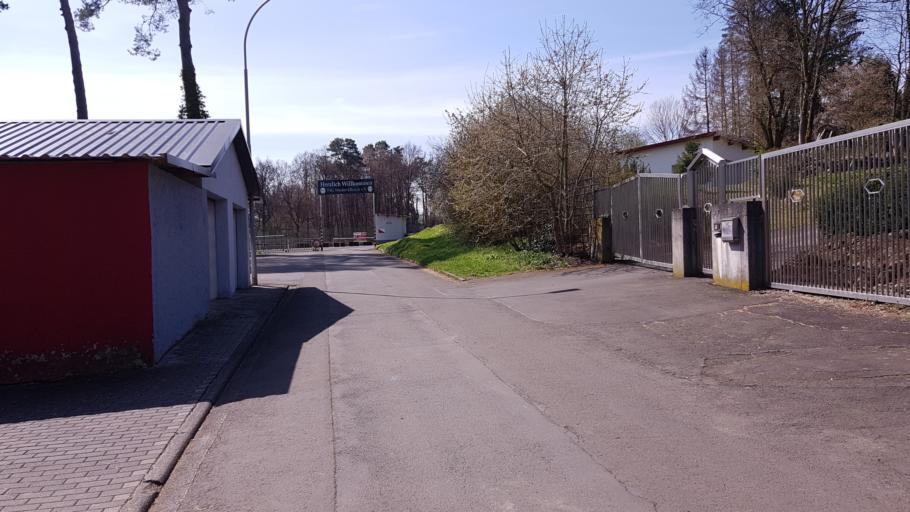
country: DE
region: Hesse
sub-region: Regierungsbezirk Giessen
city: Grunberg
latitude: 50.6410
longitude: 9.0338
